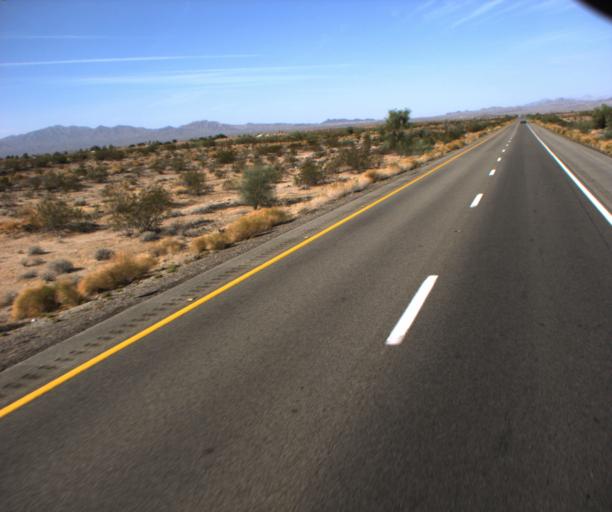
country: US
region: Arizona
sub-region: Mohave County
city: Desert Hills
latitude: 34.7645
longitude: -114.2035
